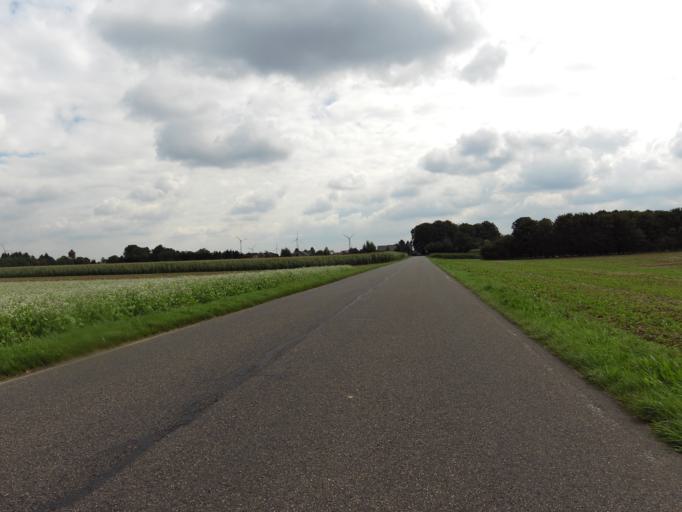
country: DE
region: North Rhine-Westphalia
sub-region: Regierungsbezirk Koln
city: Heinsberg
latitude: 51.0113
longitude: 6.0840
